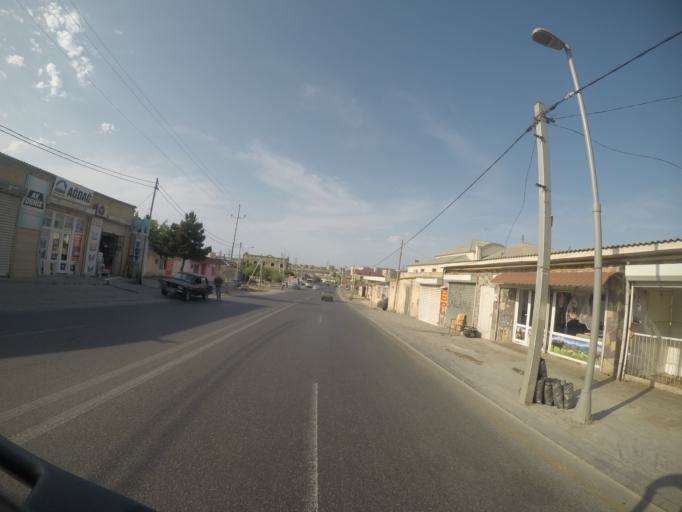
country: AZ
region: Baki
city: Binagadi
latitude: 40.4771
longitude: 49.8334
